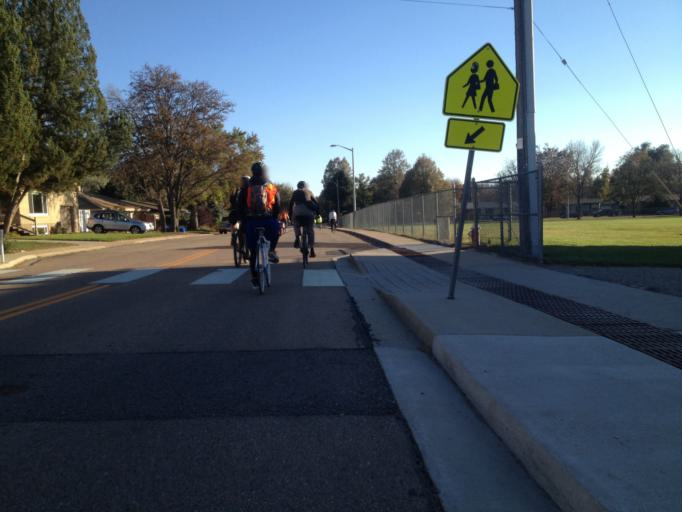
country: US
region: Colorado
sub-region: Boulder County
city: Longmont
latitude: 40.1832
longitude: -105.1145
